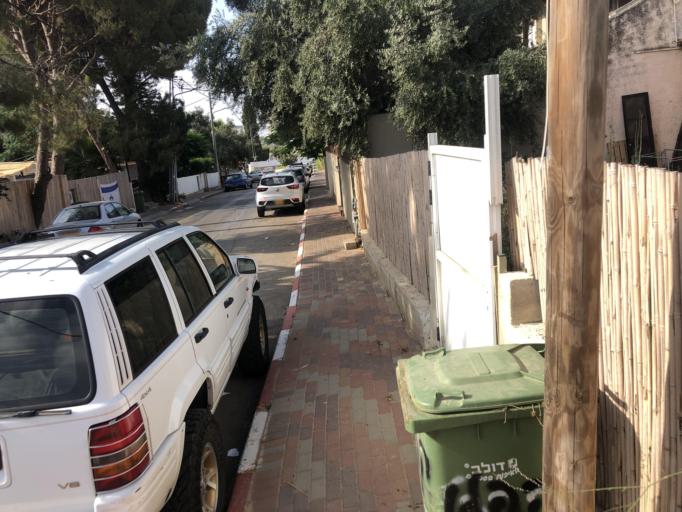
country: IL
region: Central District
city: Yehud
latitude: 32.0389
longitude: 34.8901
